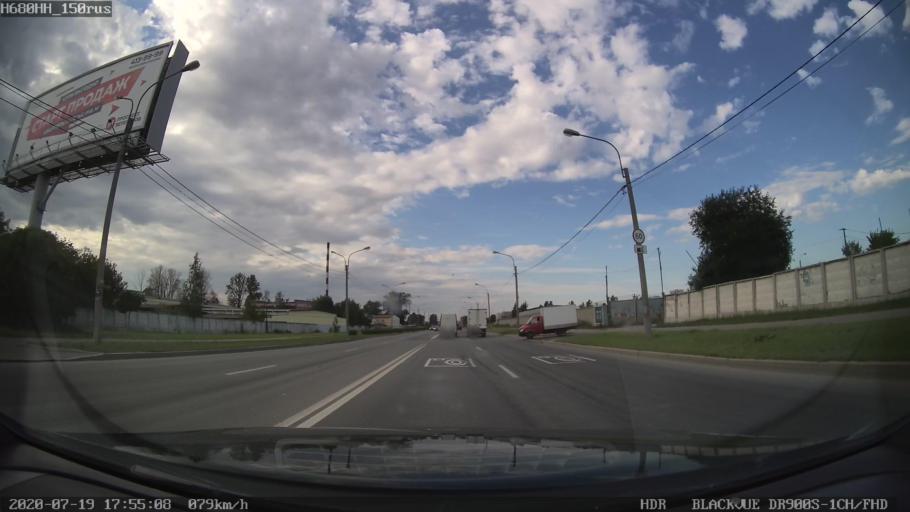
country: RU
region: St.-Petersburg
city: Admiralteisky
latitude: 59.8921
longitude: 30.3017
